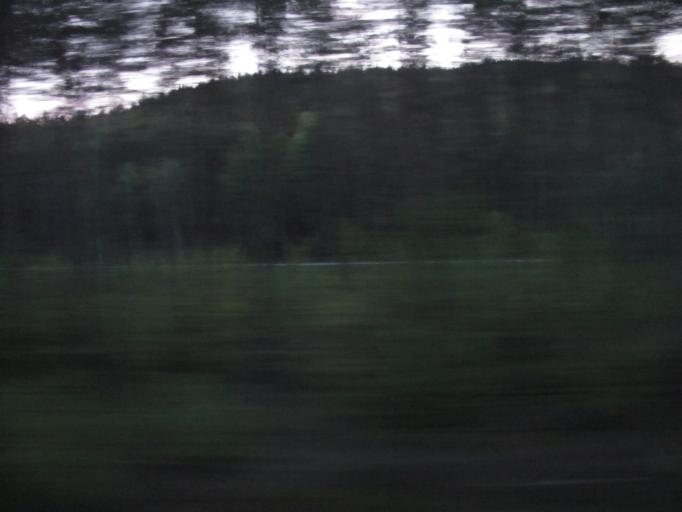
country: NO
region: Oppland
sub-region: Ringebu
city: Ringebu
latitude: 61.5485
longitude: 10.0662
